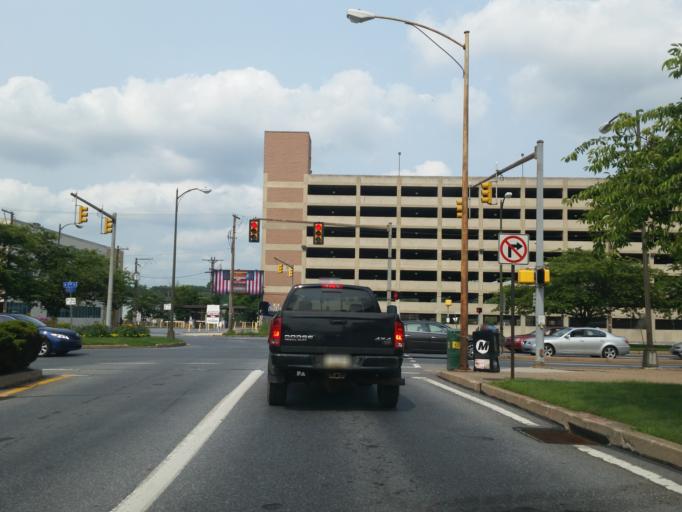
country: US
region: Pennsylvania
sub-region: Dauphin County
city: Harrisburg
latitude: 40.2682
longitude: -76.8820
